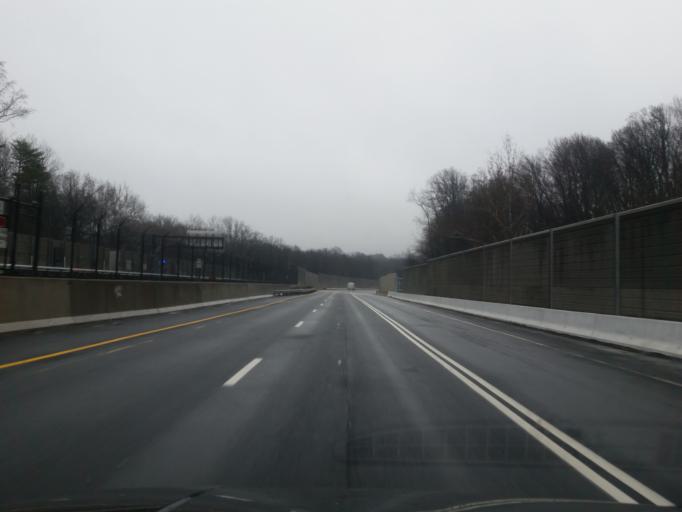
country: US
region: Virginia
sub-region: Fairfax County
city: Pimmit Hills
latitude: 38.9140
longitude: -77.1897
